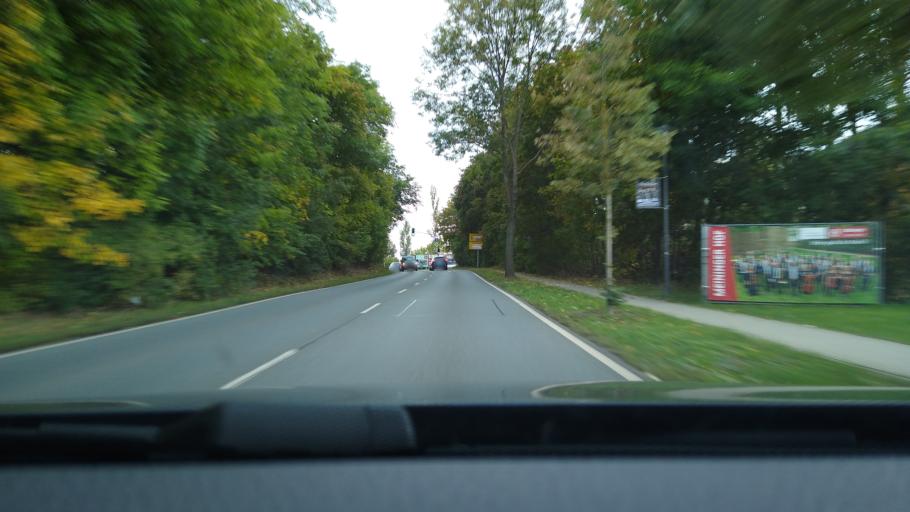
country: DE
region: Thuringia
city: Saalfeld
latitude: 50.6541
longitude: 11.3507
